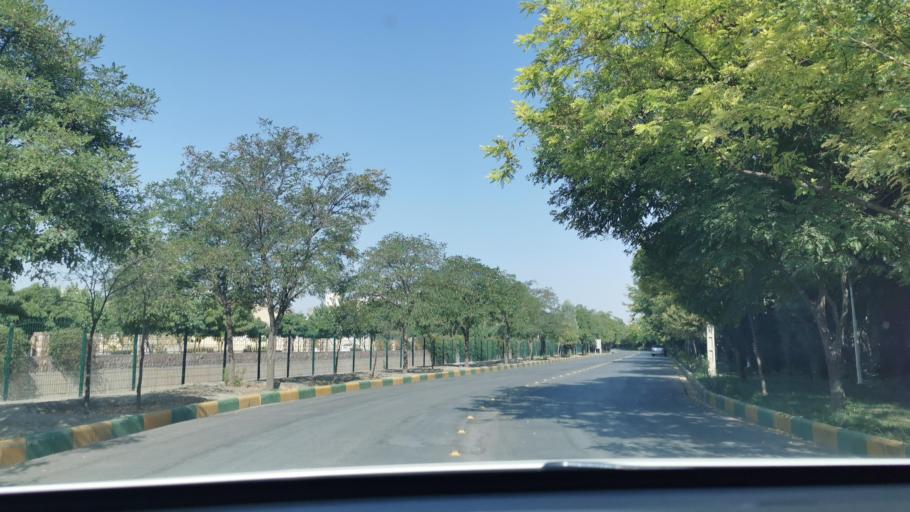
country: IR
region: Razavi Khorasan
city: Mashhad
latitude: 36.3285
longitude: 59.6379
